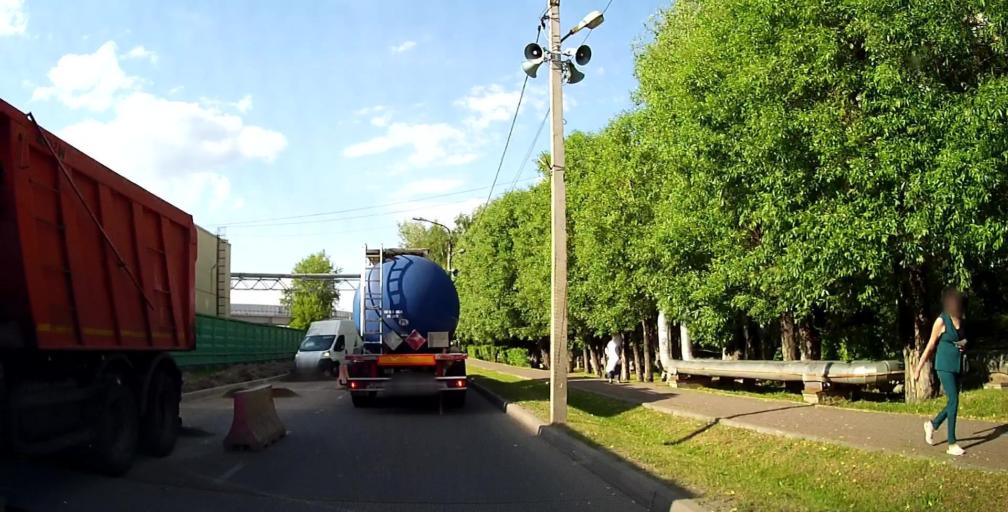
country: RU
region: Moskovskaya
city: Shcherbinka
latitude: 55.5058
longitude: 37.5623
